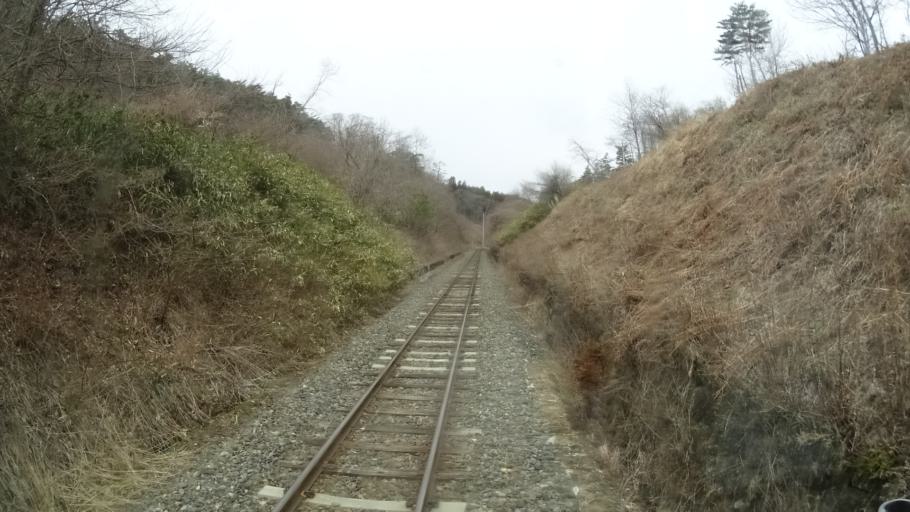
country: JP
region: Iwate
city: Tono
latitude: 39.3213
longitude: 141.3668
